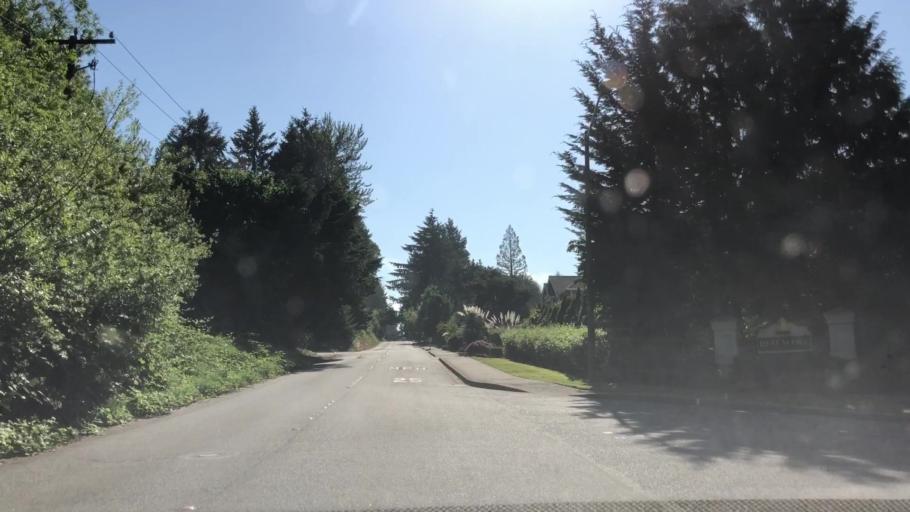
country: US
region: Washington
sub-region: King County
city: Eastgate
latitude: 47.6152
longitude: -122.1395
